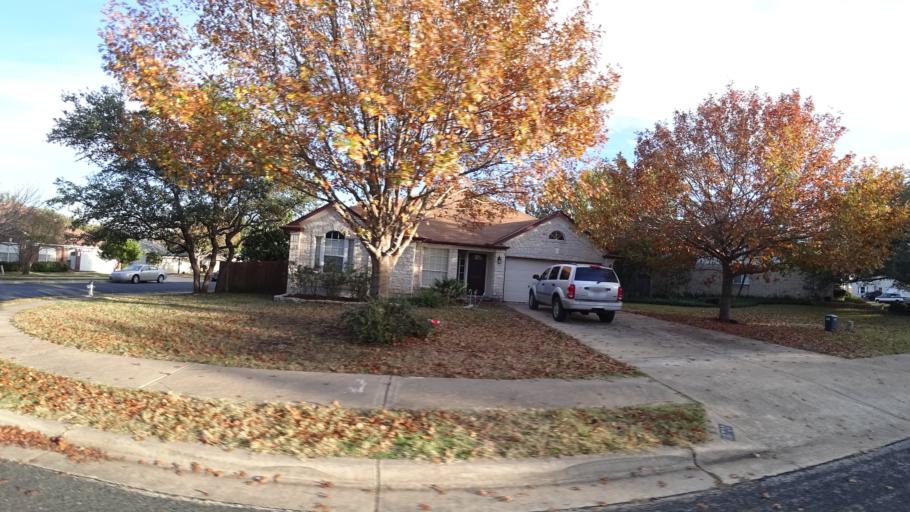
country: US
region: Texas
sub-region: Williamson County
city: Brushy Creek
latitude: 30.5040
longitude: -97.7361
